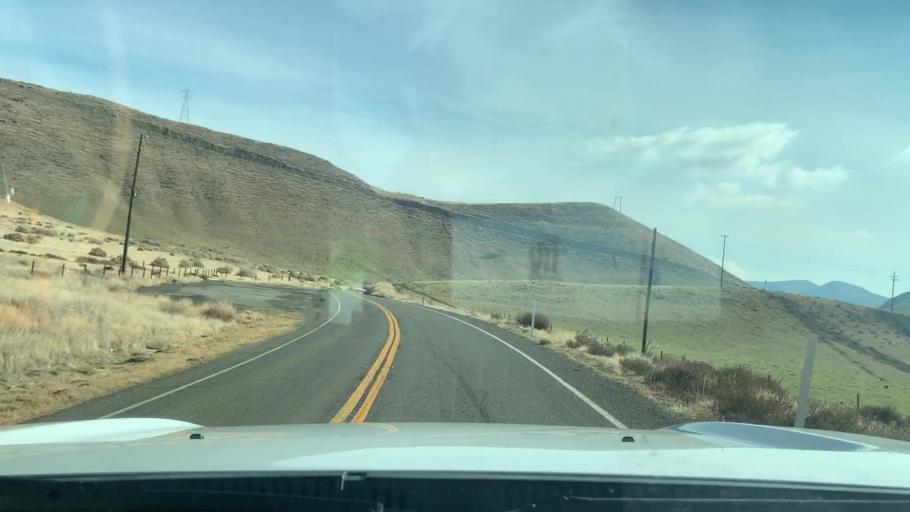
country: US
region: California
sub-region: Fresno County
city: Coalinga
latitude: 36.0967
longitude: -120.4390
